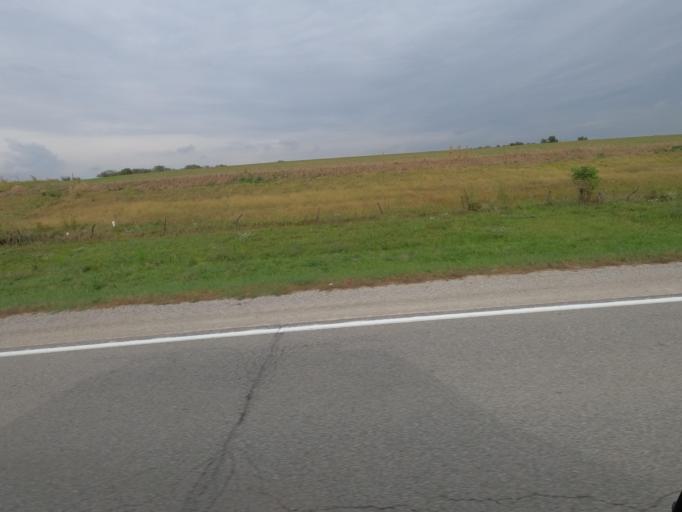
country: US
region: Iowa
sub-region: Van Buren County
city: Keosauqua
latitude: 40.8611
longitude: -92.1307
